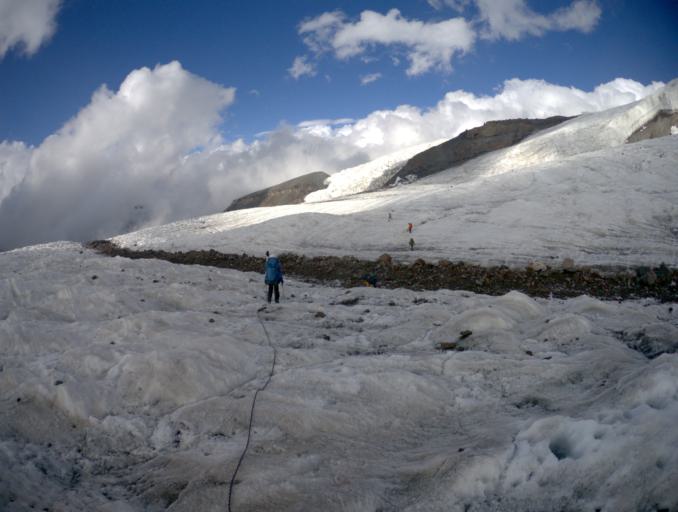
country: RU
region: Kabardino-Balkariya
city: Terskol
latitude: 43.3852
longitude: 42.4256
